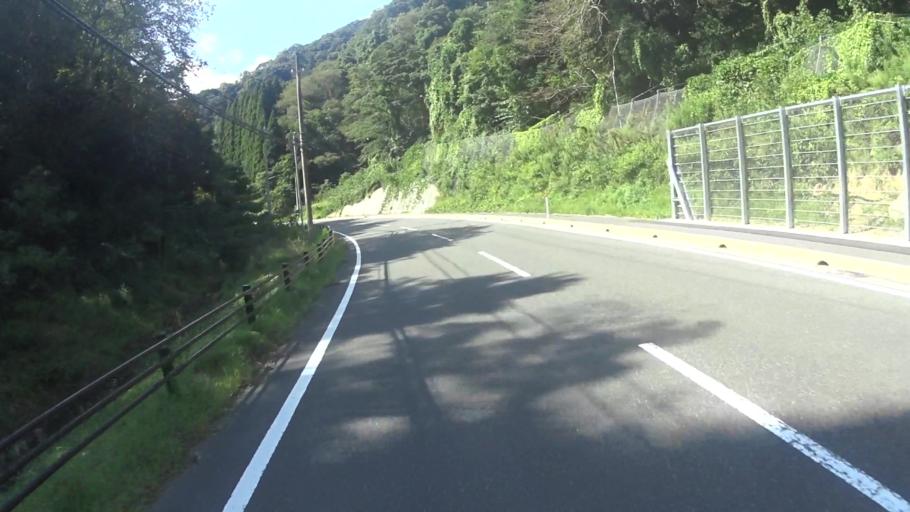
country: JP
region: Kyoto
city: Miyazu
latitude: 35.6871
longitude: 135.2887
